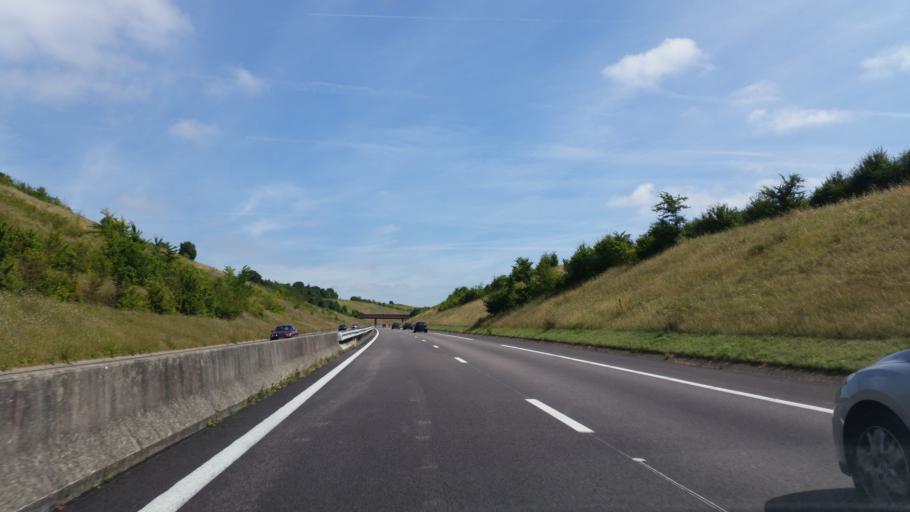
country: FR
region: Haute-Normandie
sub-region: Departement de la Seine-Maritime
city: Gaillefontaine
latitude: 49.7373
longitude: 1.5729
